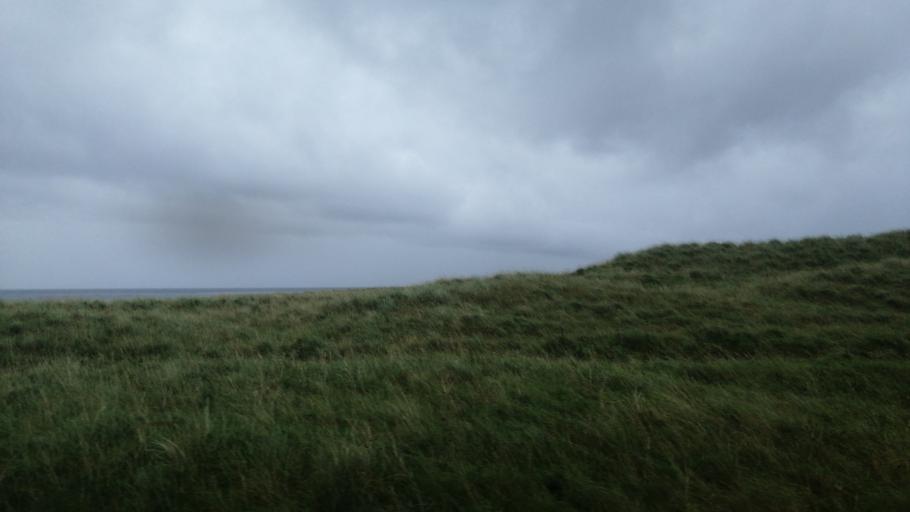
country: GB
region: Scotland
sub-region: Highland
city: Brora
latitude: 58.0824
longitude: -3.7212
